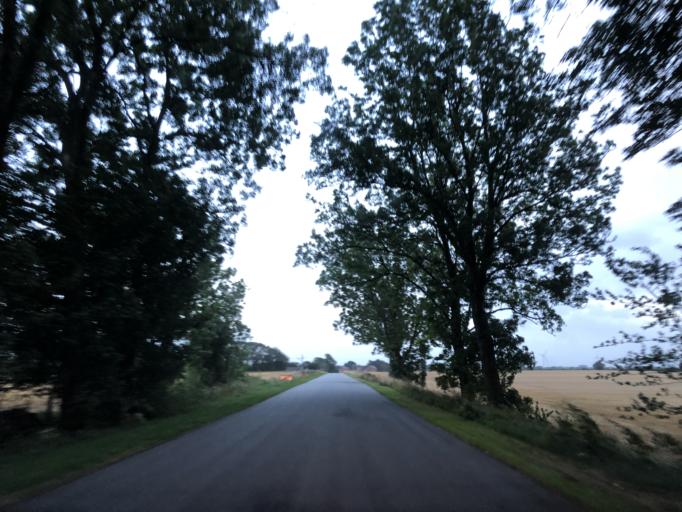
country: DK
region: South Denmark
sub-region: Haderslev Kommune
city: Starup
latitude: 55.2506
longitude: 9.6403
